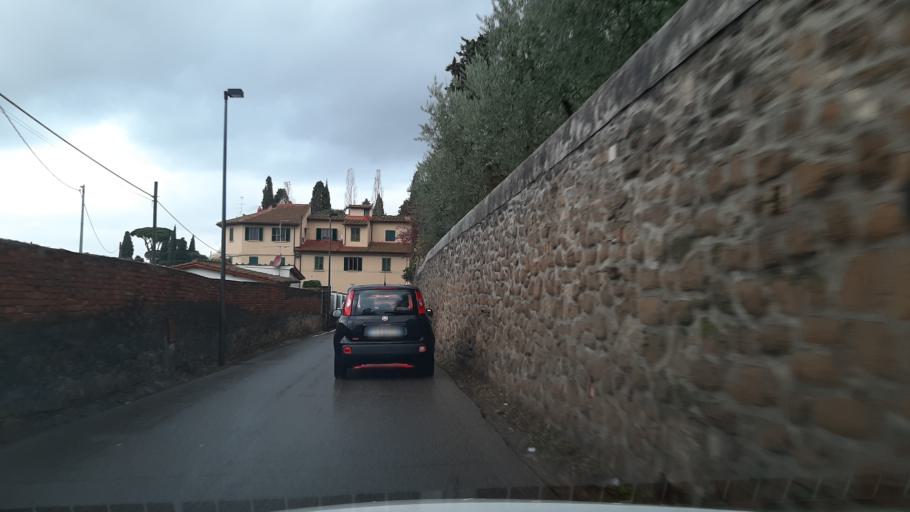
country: IT
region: Tuscany
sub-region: Province of Florence
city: Florence
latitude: 43.8101
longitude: 11.2577
